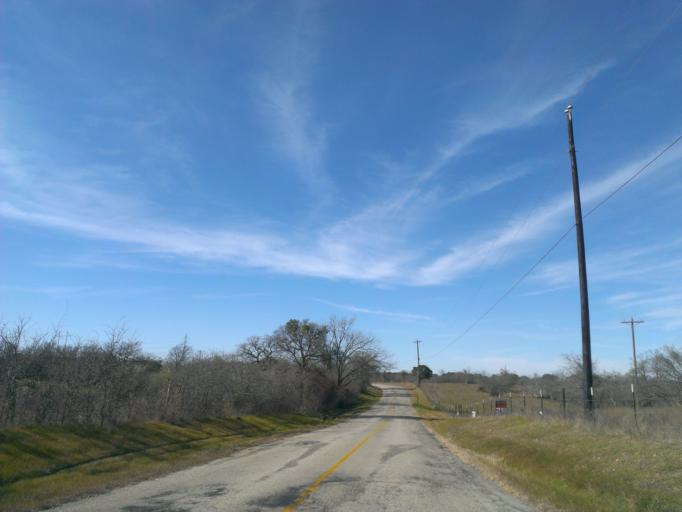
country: US
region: Texas
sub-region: Burnet County
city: Marble Falls
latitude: 30.5098
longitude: -98.2033
